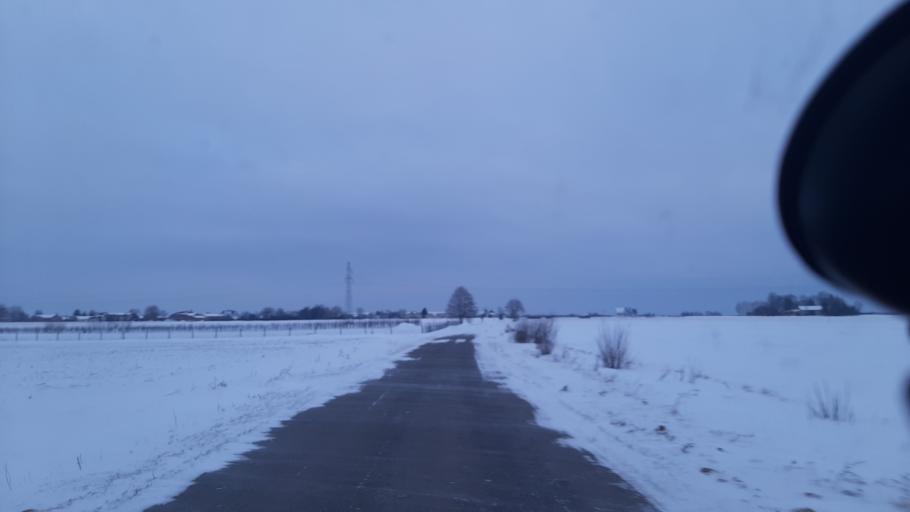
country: PL
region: Lublin Voivodeship
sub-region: Powiat lubelski
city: Jastkow
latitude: 51.3482
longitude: 22.4081
